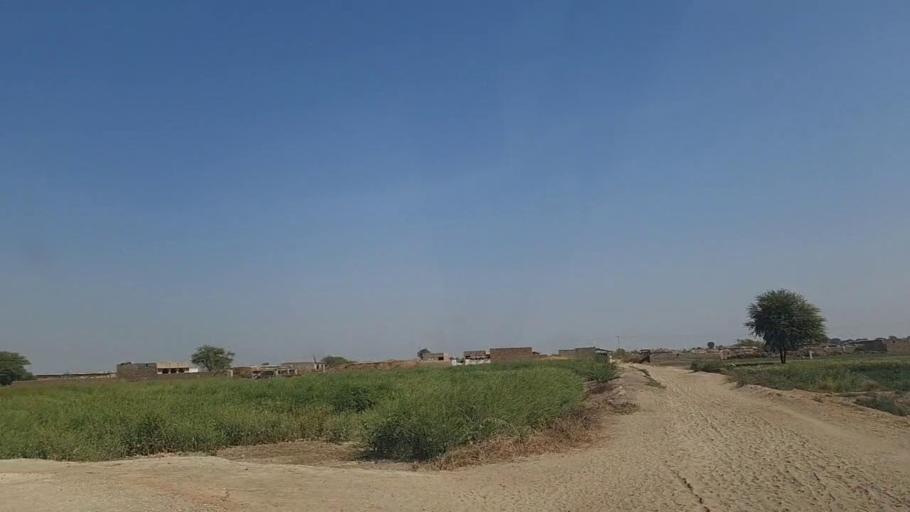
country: PK
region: Sindh
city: Naukot
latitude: 24.8733
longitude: 69.4081
